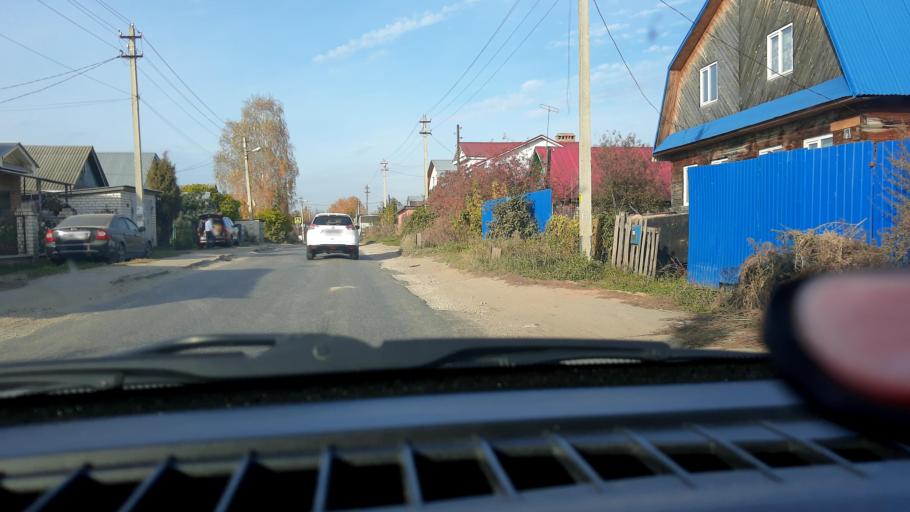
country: RU
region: Nizjnij Novgorod
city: Neklyudovo
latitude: 56.4085
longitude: 43.9804
